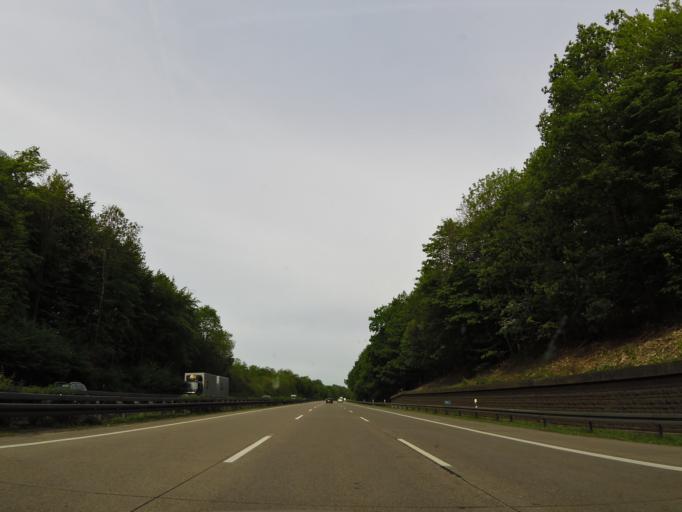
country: DE
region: Lower Saxony
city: Schellerten
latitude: 52.1209
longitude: 10.0914
